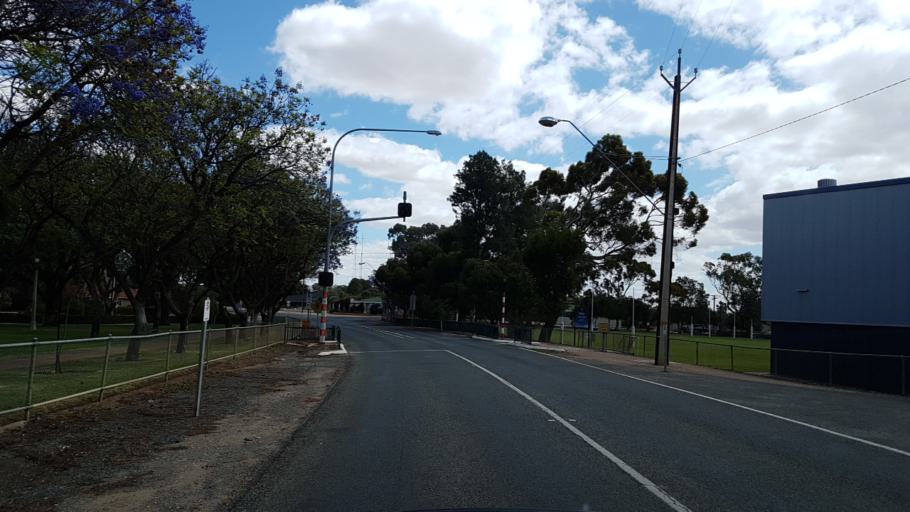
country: AU
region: South Australia
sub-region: Loxton Waikerie
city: Waikerie
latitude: -34.1819
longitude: 139.9823
